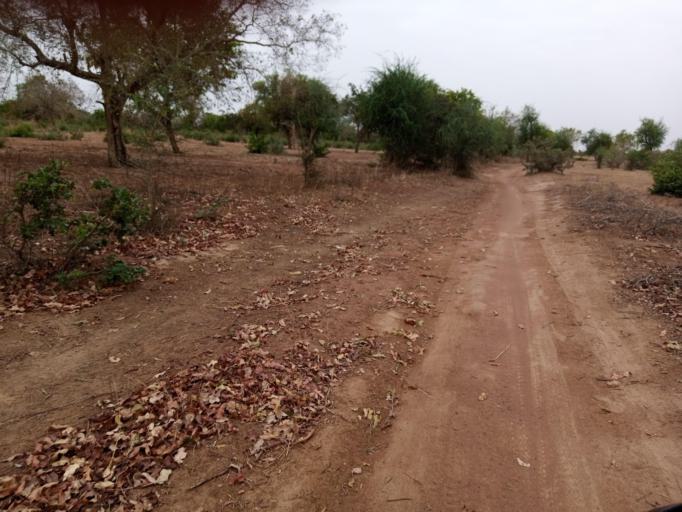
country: BF
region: Boucle du Mouhoun
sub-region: Province de la Kossi
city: Nouna
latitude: 12.8344
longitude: -4.0772
